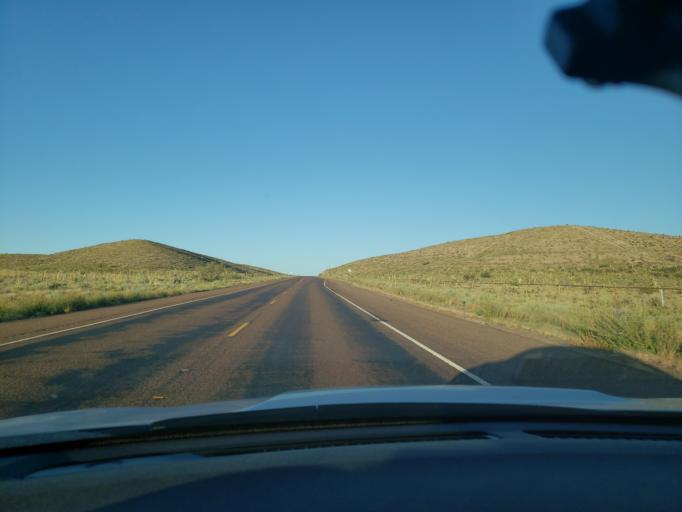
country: US
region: Texas
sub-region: El Paso County
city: Homestead Meadows South
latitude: 31.8269
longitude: -105.8977
